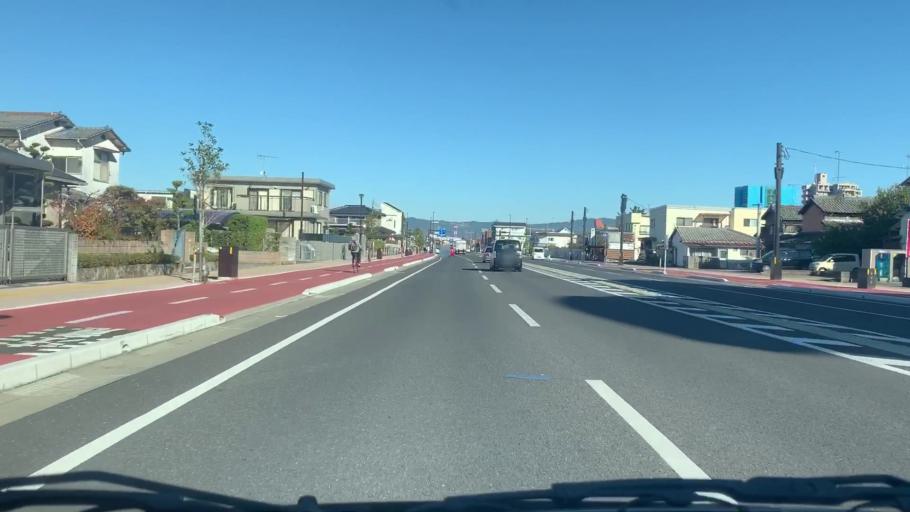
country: JP
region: Saga Prefecture
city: Saga-shi
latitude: 33.2468
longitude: 130.2929
